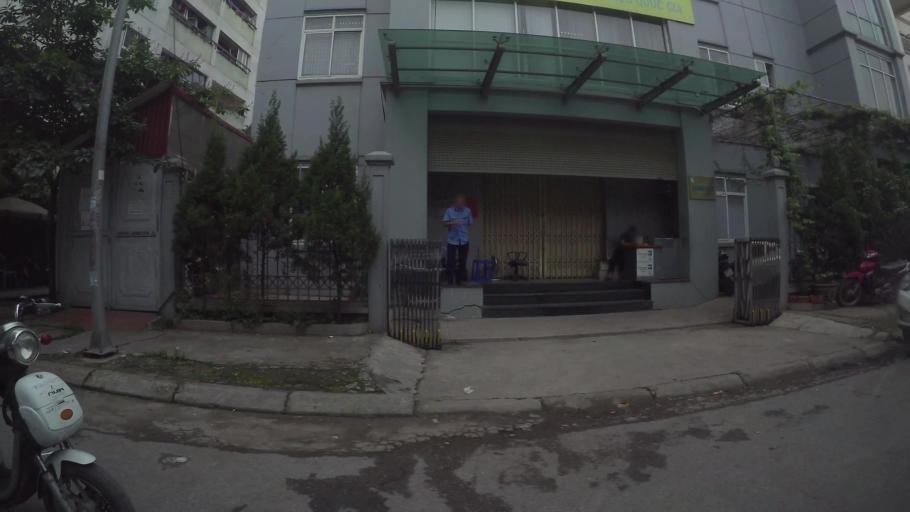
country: VN
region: Ha Noi
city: Hai BaTrung
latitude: 20.9844
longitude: 105.8658
